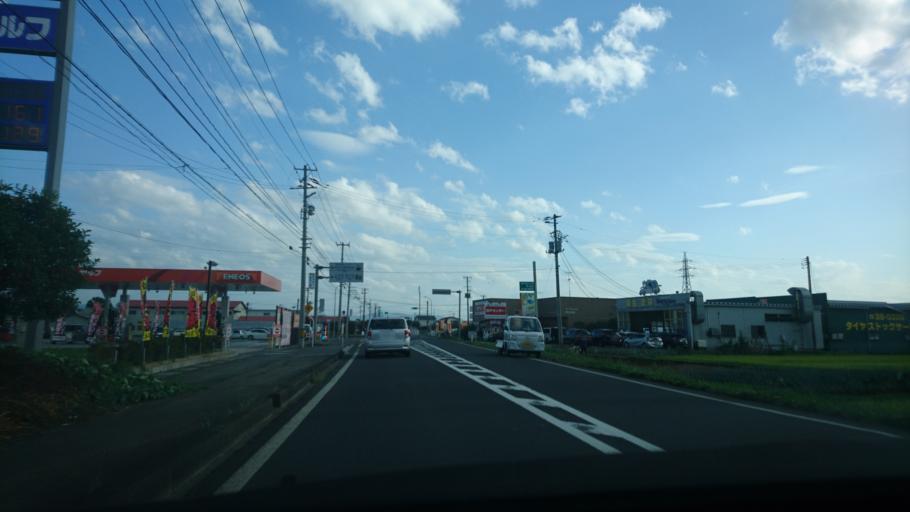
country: JP
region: Iwate
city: Mizusawa
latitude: 39.1599
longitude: 141.1803
